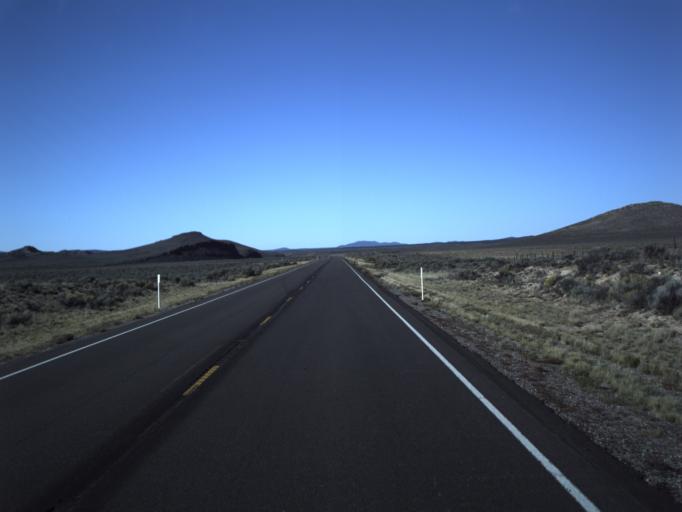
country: US
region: Utah
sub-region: Washington County
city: Enterprise
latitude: 37.8000
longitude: -113.9313
